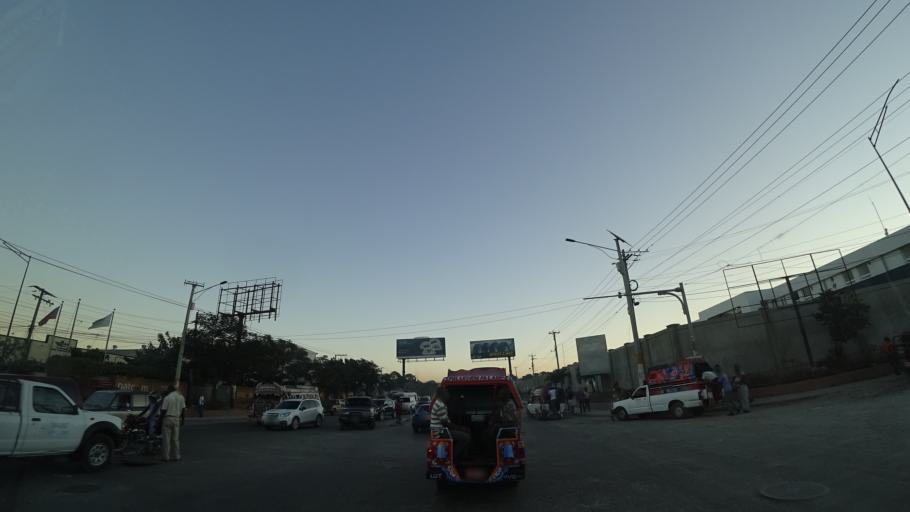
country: HT
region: Ouest
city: Delmas 73
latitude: 18.5679
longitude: -72.3111
